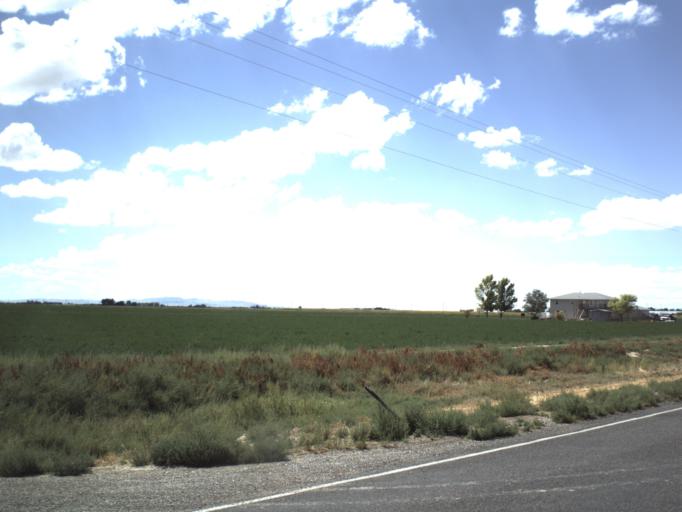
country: US
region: Utah
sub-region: Millard County
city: Delta
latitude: 39.3529
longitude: -112.5364
